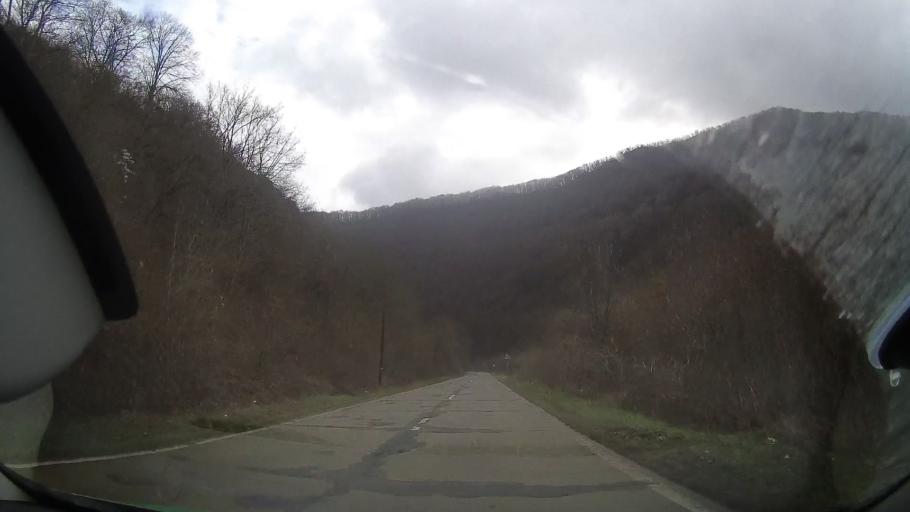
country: RO
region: Alba
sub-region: Comuna Rimetea
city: Rimetea
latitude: 46.5049
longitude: 23.5743
